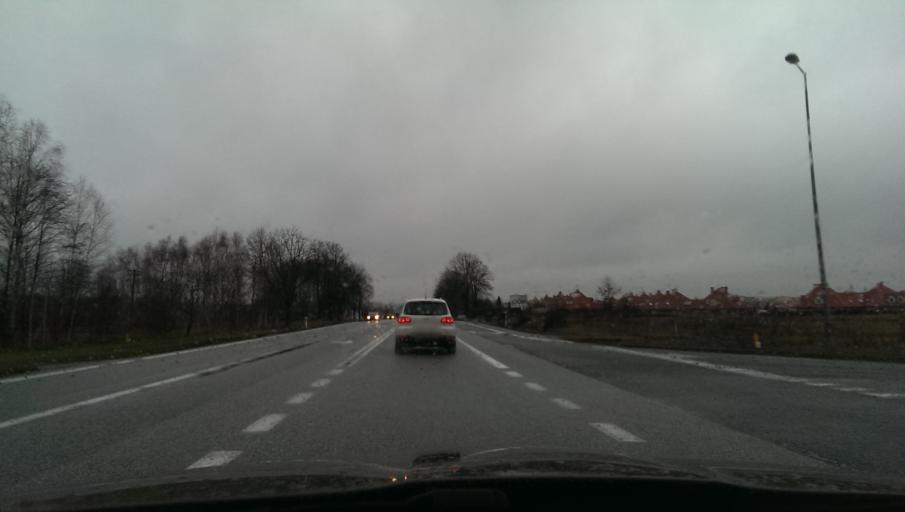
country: PL
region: Subcarpathian Voivodeship
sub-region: Powiat rzeszowski
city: Glogow Malopolski
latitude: 50.1338
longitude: 21.9660
